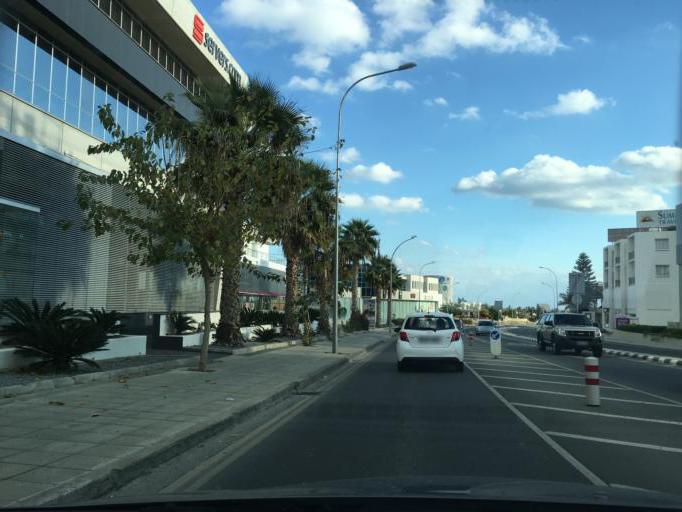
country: CY
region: Limassol
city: Limassol
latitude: 34.6984
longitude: 33.0632
